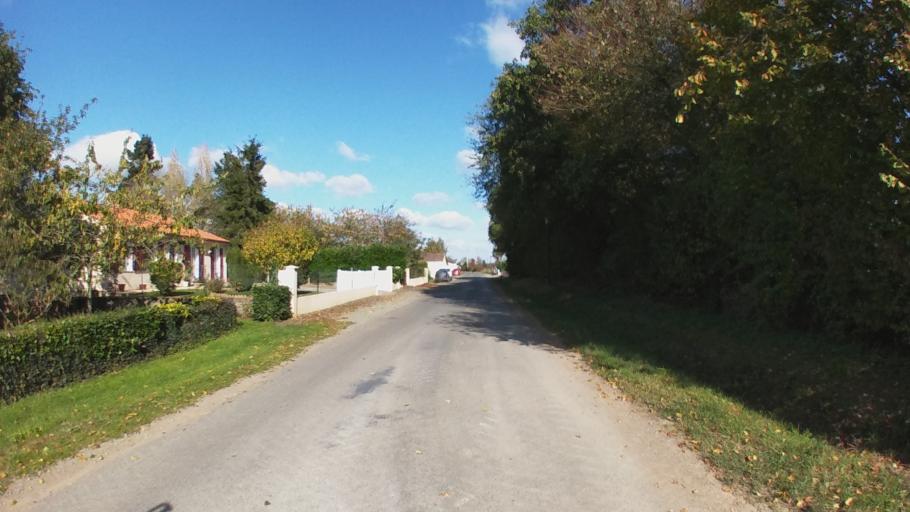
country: FR
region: Pays de la Loire
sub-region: Departement de la Vendee
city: Les Magnils-Reigniers
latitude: 46.5008
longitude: -1.2166
